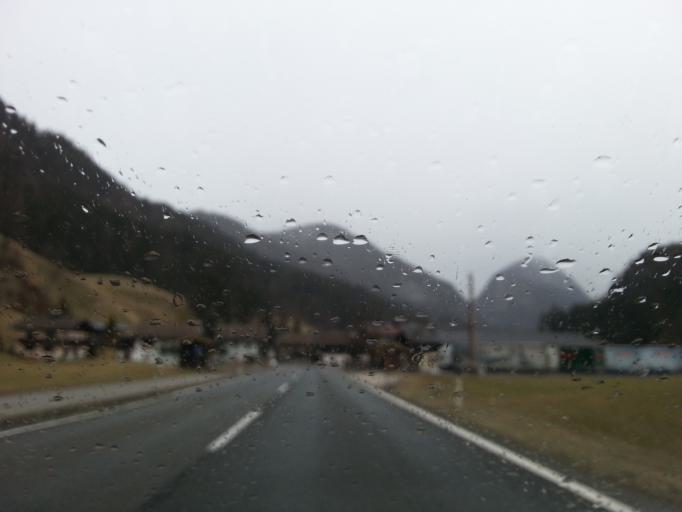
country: AT
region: Salzburg
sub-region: Politischer Bezirk Zell am See
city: Lofer
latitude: 47.6144
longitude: 12.7053
